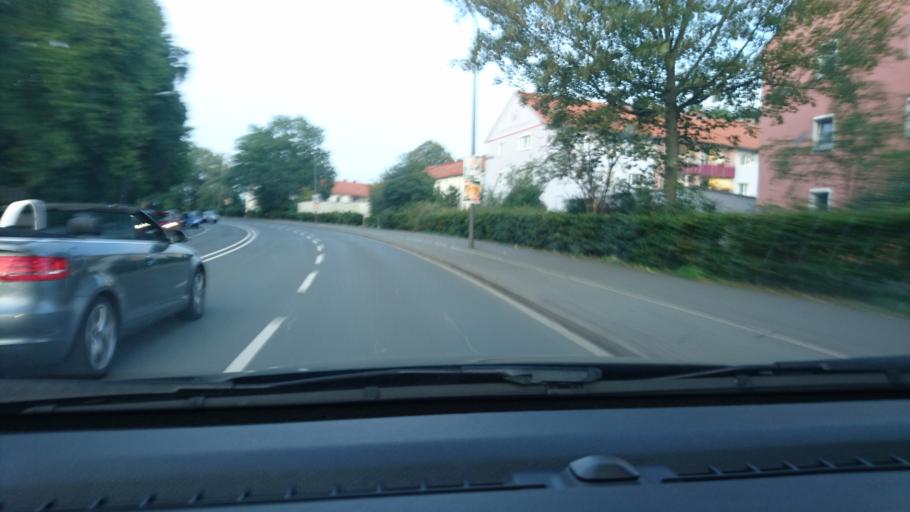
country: DE
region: Bavaria
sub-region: Upper Franconia
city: Bayreuth
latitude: 49.9490
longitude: 11.5966
